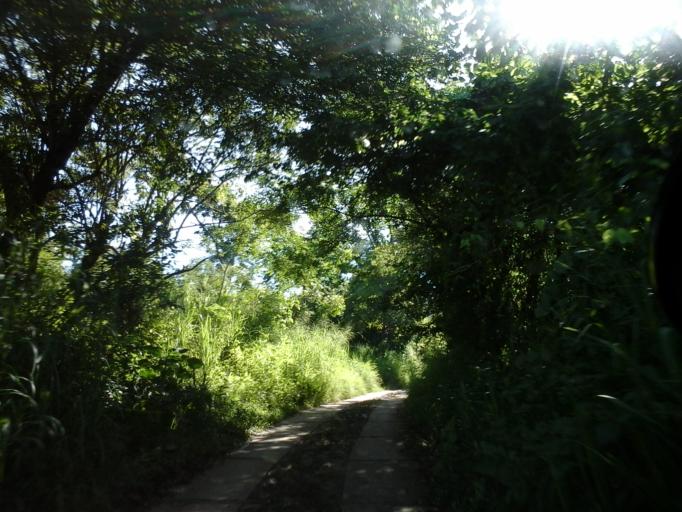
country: CO
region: Cesar
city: San Diego
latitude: 10.2696
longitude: -73.0969
